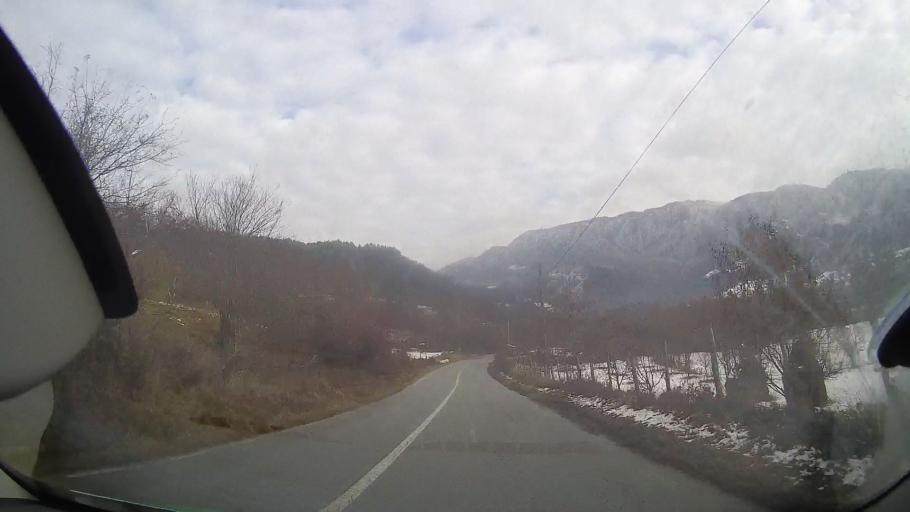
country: RO
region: Alba
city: Salciua de Sus
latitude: 46.4032
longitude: 23.4332
